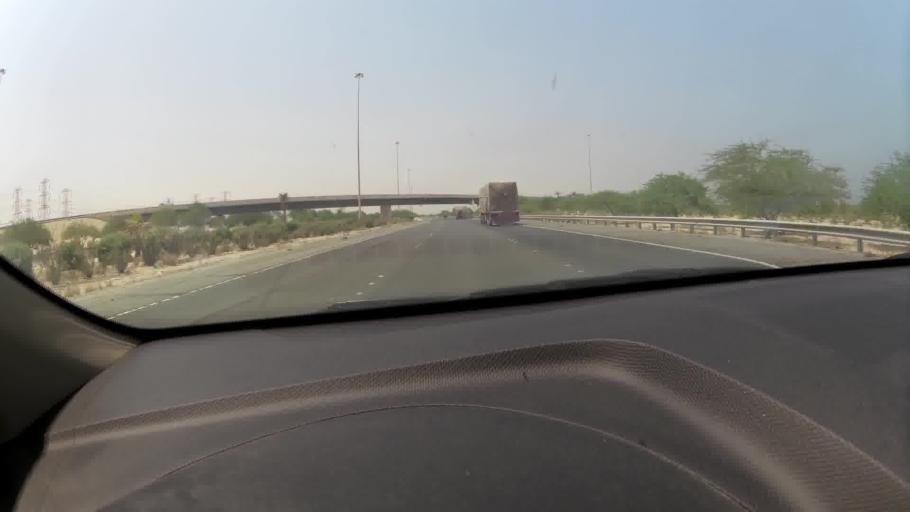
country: KW
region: Al Ahmadi
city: Al Fahahil
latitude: 28.9191
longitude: 48.2059
